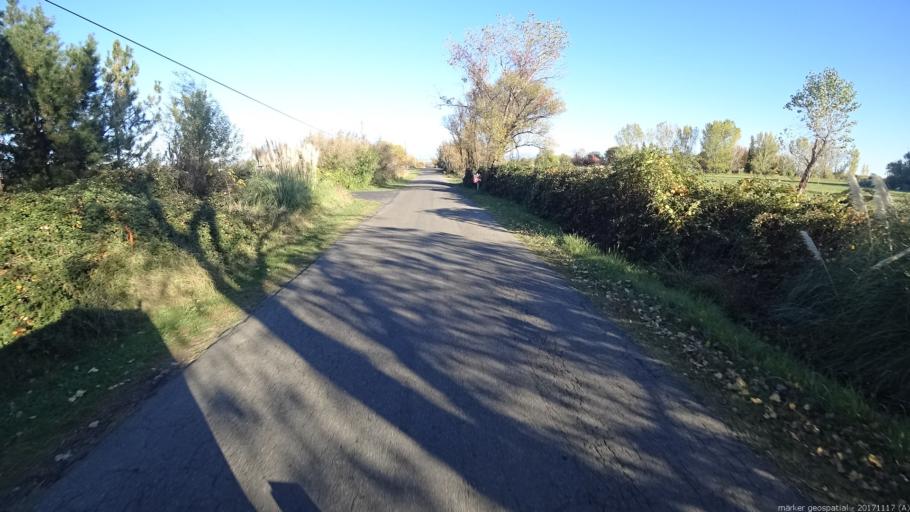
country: US
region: California
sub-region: Shasta County
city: Cottonwood
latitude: 40.4162
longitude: -122.2439
